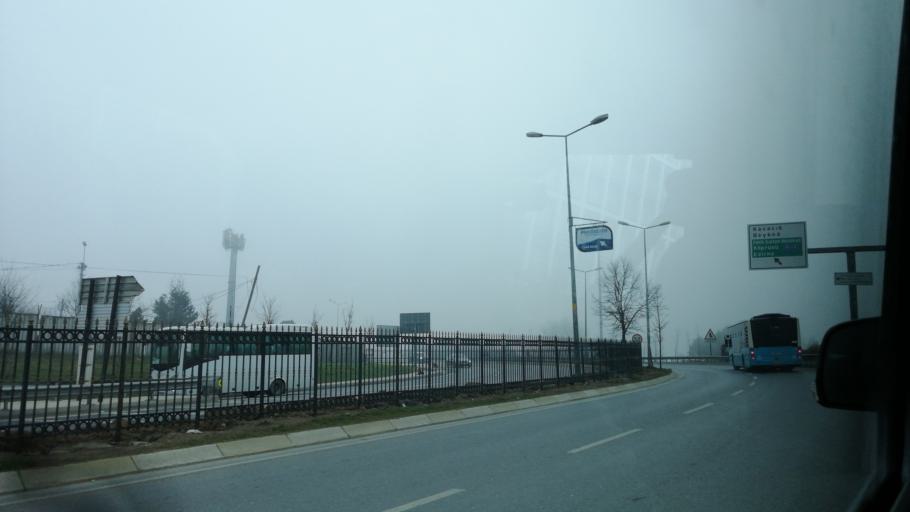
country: TR
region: Istanbul
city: Umraniye
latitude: 41.0885
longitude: 29.0888
